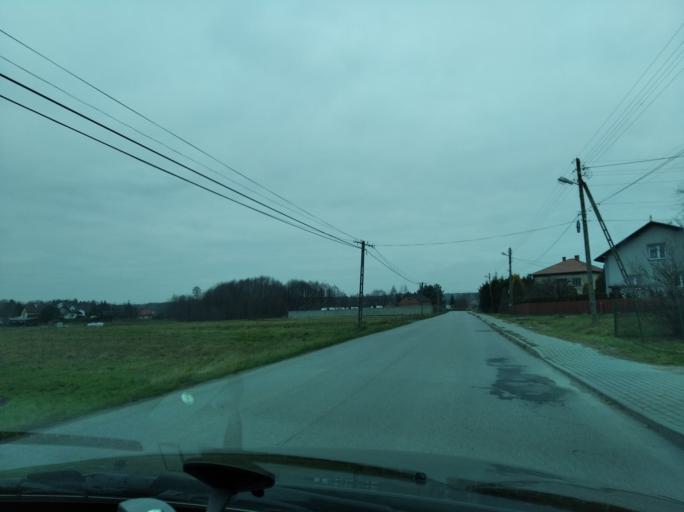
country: PL
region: Subcarpathian Voivodeship
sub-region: Powiat lancucki
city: Rakszawa
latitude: 50.1649
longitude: 22.2356
